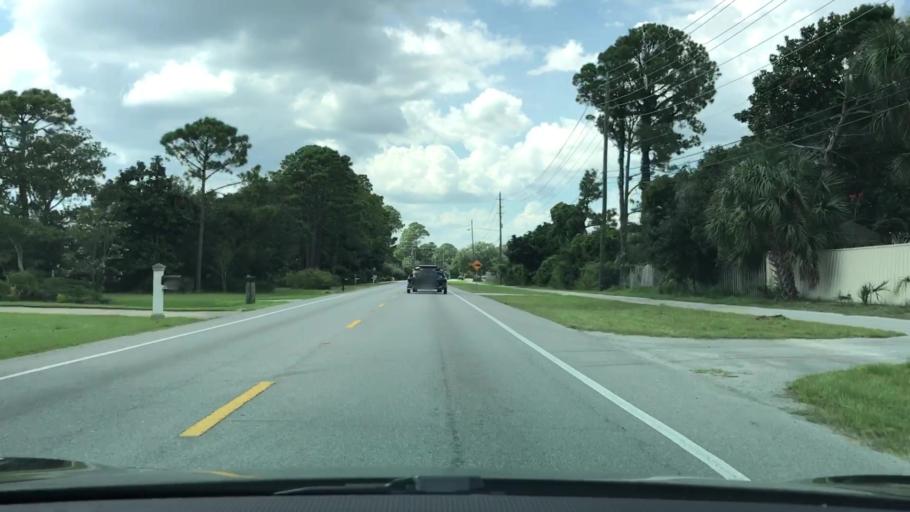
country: US
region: Florida
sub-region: Bay County
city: Panama City Beach
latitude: 30.1693
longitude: -85.7842
